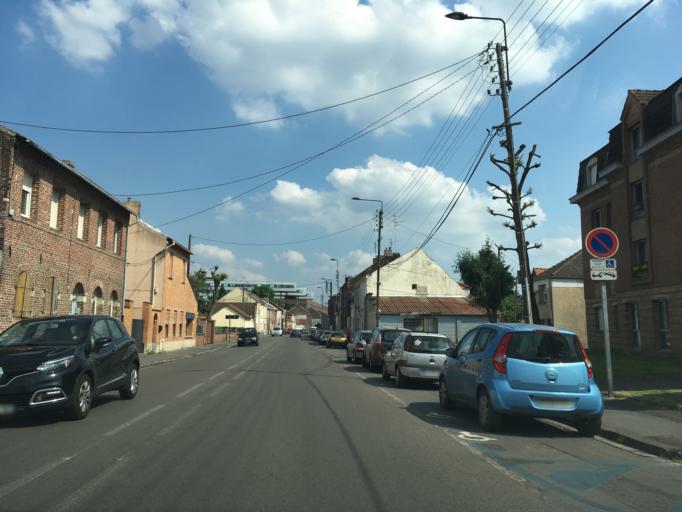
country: FR
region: Nord-Pas-de-Calais
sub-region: Departement du Nord
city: Petite-Foret
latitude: 50.3621
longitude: 3.4943
